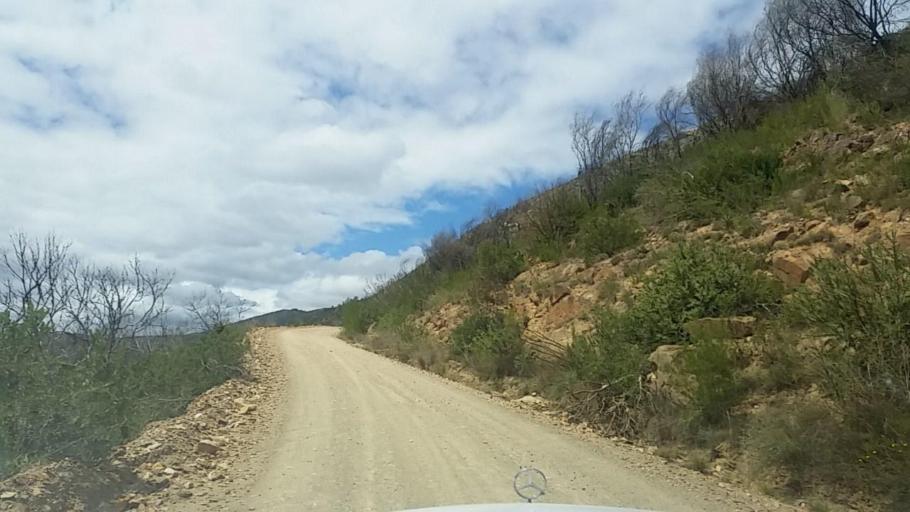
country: ZA
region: Western Cape
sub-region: Eden District Municipality
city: Knysna
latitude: -33.8200
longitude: 23.1756
